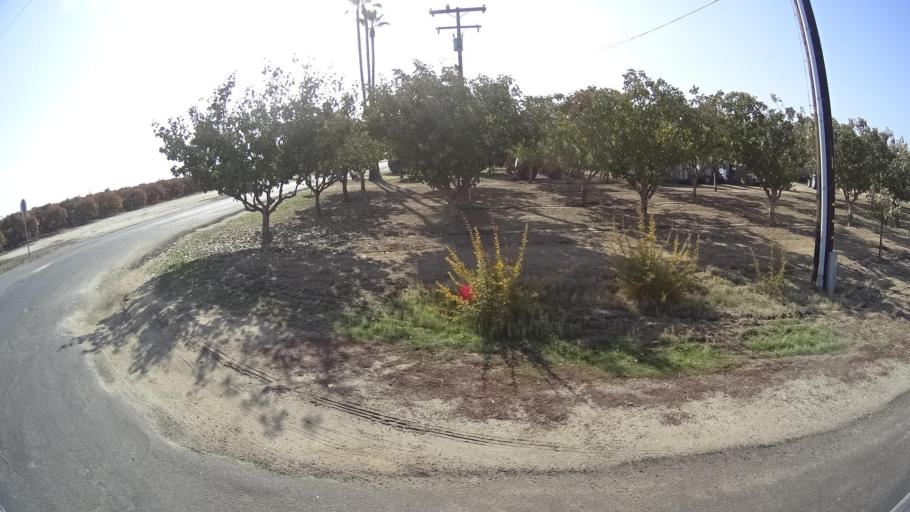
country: US
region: California
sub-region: Kern County
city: McFarland
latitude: 35.6891
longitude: -119.1693
